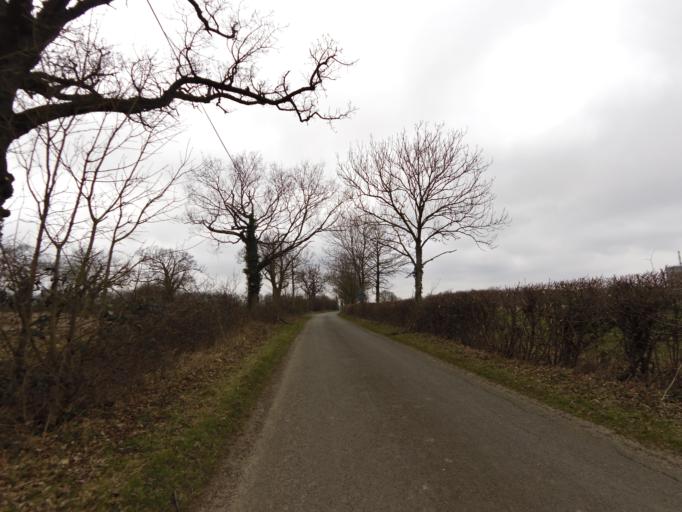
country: GB
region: England
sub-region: Suffolk
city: Cookley
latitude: 52.2909
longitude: 1.4677
